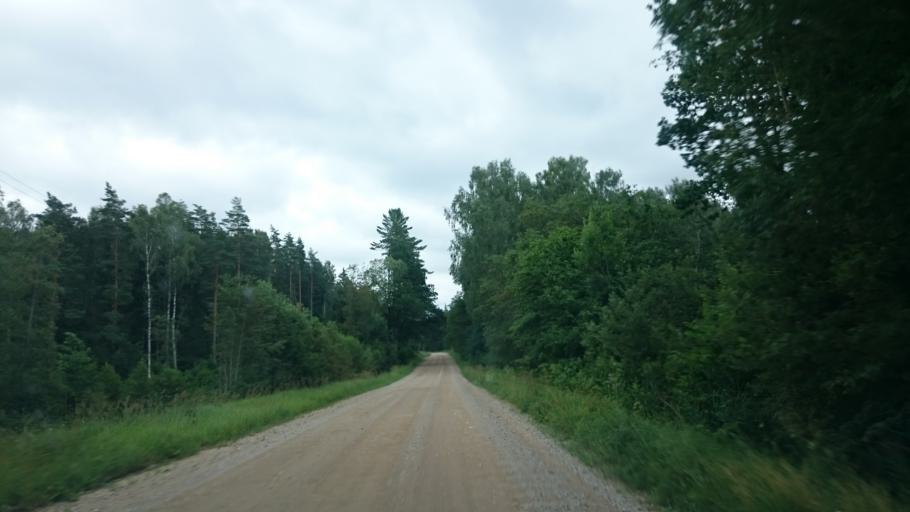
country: LV
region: Durbe
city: Liegi
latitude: 56.7564
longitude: 21.3328
